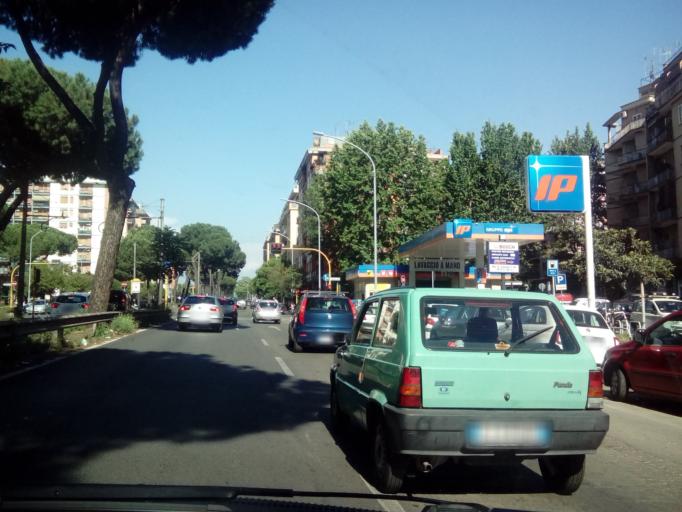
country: IT
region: Latium
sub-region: Citta metropolitana di Roma Capitale
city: Rome
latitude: 41.8949
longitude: 12.5623
